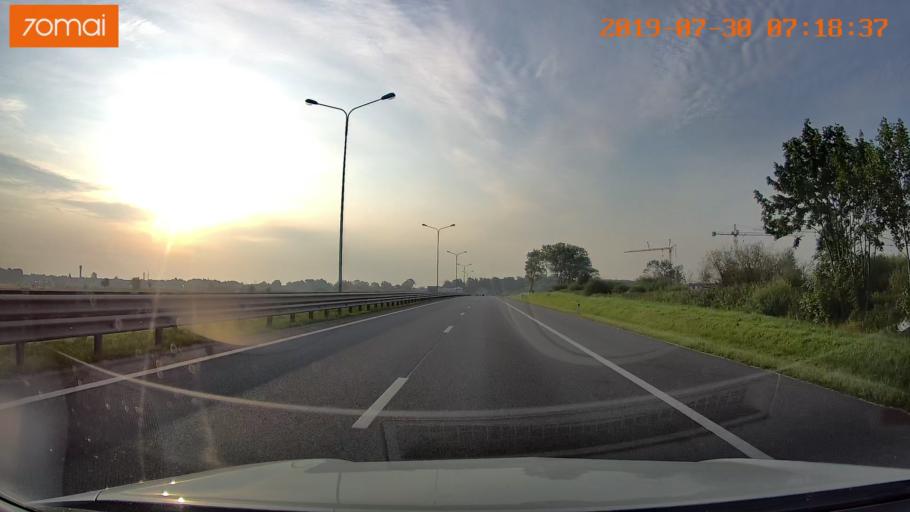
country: RU
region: Kaliningrad
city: Bol'shoe Isakovo
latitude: 54.7033
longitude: 20.6525
